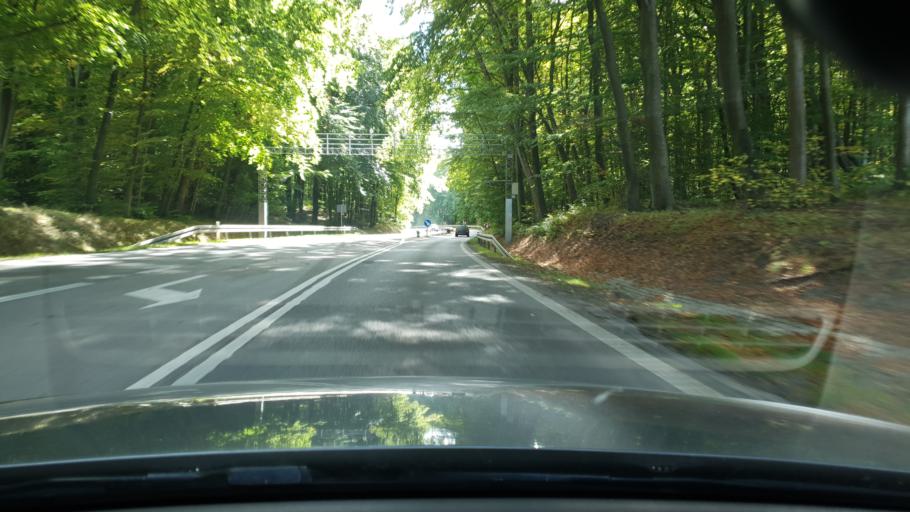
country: PL
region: Pomeranian Voivodeship
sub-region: Powiat wejherowski
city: Rekowo Dolne
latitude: 54.6335
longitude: 18.3448
